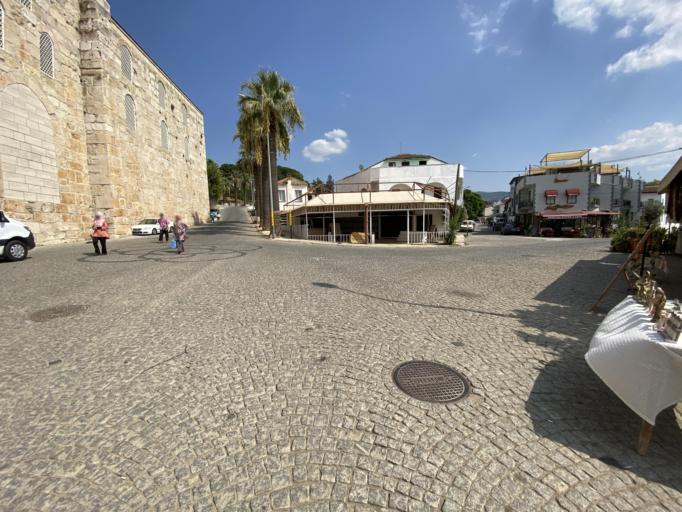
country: TR
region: Izmir
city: Selcuk
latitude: 37.9520
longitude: 27.3656
